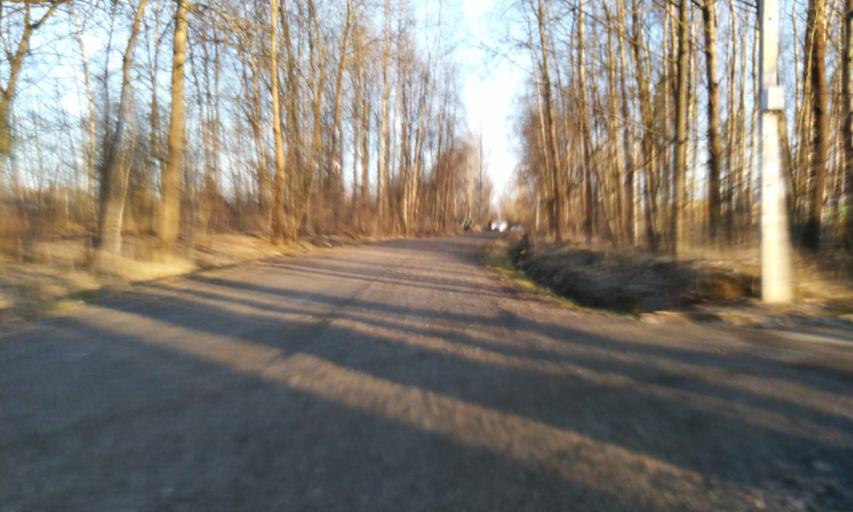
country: RU
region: Leningrad
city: Novoye Devyatkino
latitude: 60.0871
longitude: 30.4576
